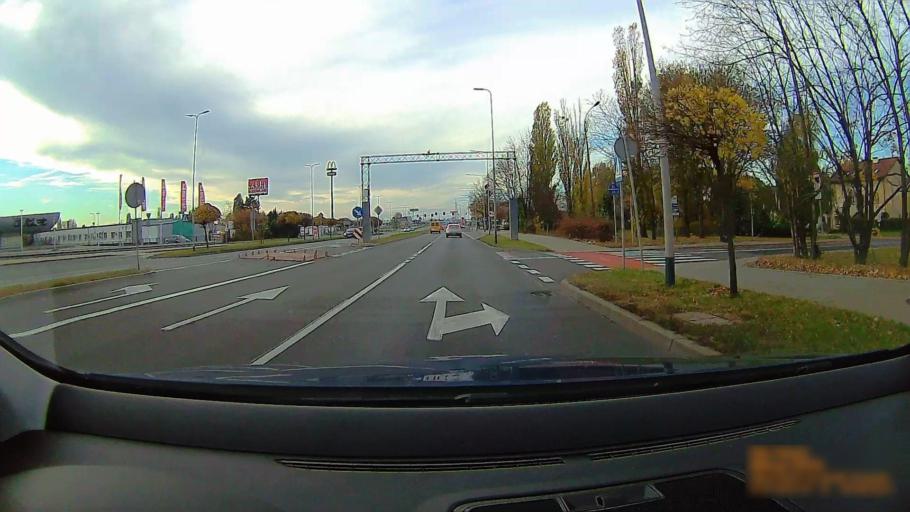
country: PL
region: Greater Poland Voivodeship
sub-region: Kalisz
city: Kalisz
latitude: 51.7436
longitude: 18.0539
